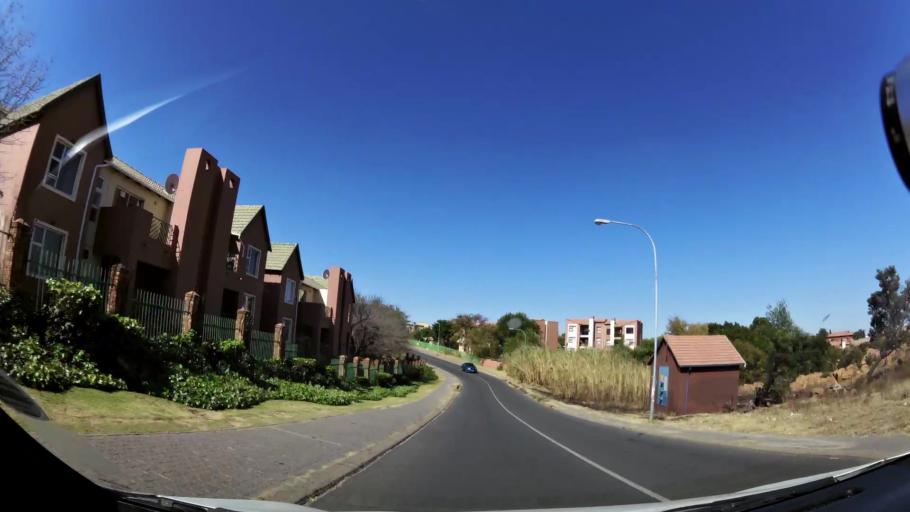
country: ZA
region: Gauteng
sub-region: City of Johannesburg Metropolitan Municipality
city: Johannesburg
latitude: -26.2681
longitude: 28.0186
